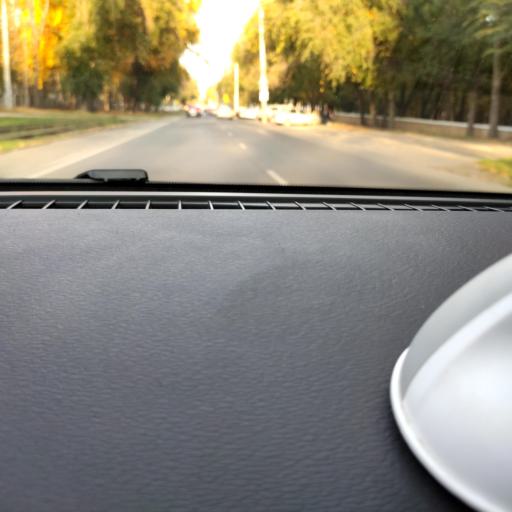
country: RU
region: Samara
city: Samara
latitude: 53.2248
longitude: 50.2387
